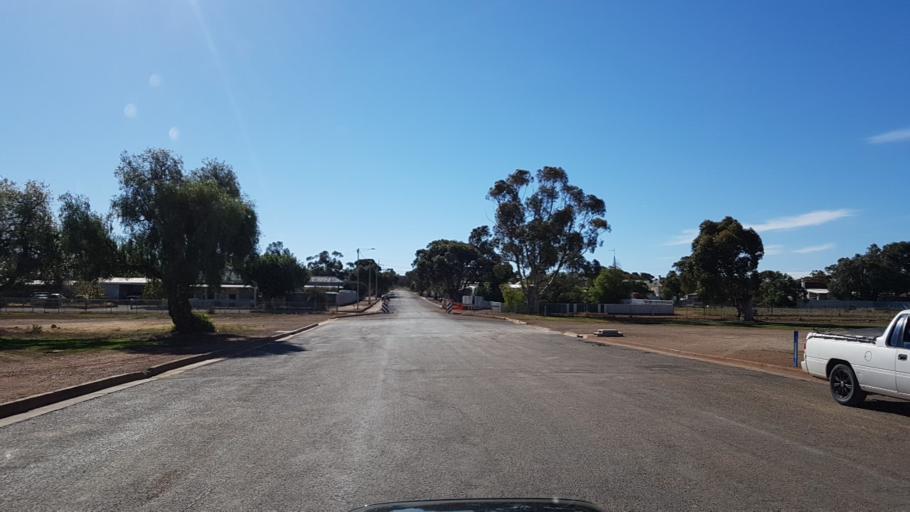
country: AU
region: South Australia
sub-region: Peterborough
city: Peterborough
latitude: -32.9717
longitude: 138.8392
